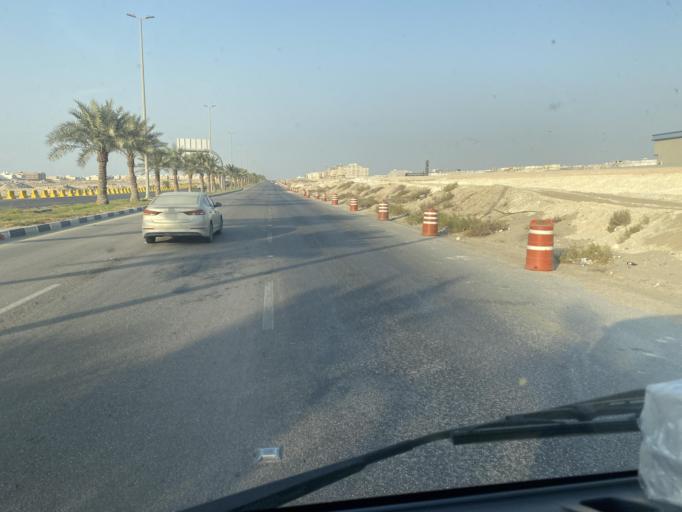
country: SA
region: Eastern Province
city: Dhahran
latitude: 26.3508
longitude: 50.0519
